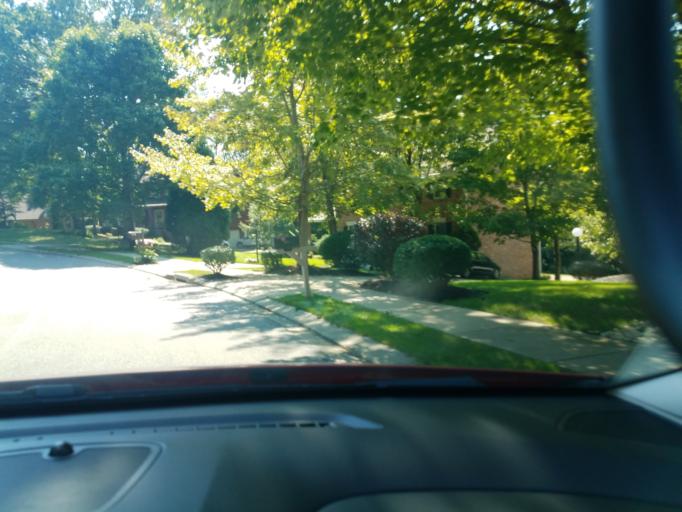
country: US
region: Pennsylvania
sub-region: Allegheny County
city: Franklin Park
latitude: 40.5592
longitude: -80.0710
